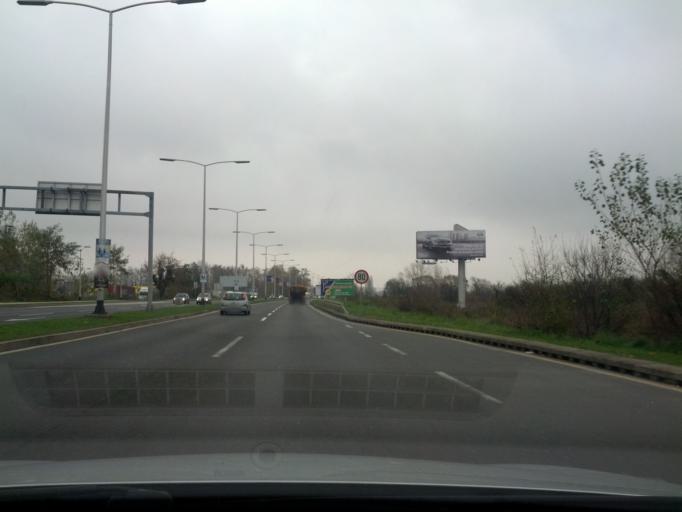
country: HR
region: Grad Zagreb
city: Jezdovec
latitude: 45.7956
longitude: 15.8628
